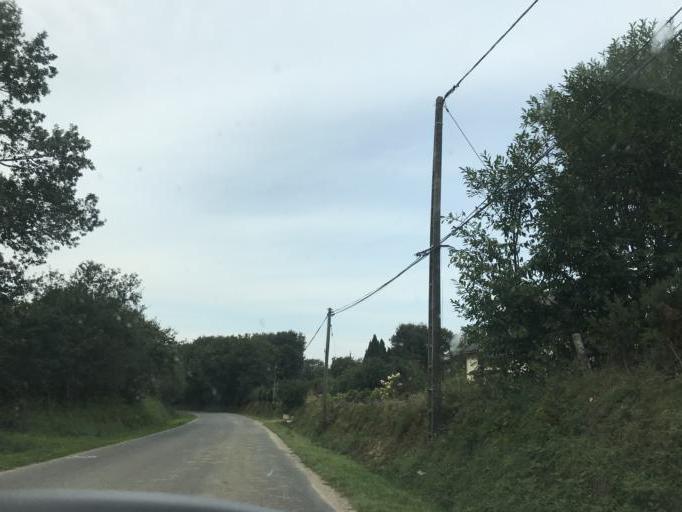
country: FR
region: Brittany
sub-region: Departement du Finistere
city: Plouneour-Menez
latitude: 48.3642
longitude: -3.8544
